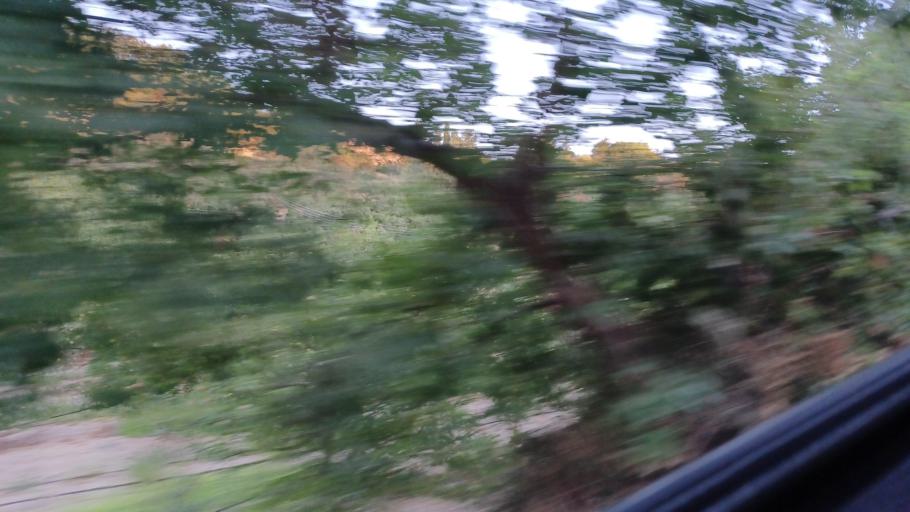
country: CY
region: Pafos
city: Tala
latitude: 34.8824
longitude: 32.4797
